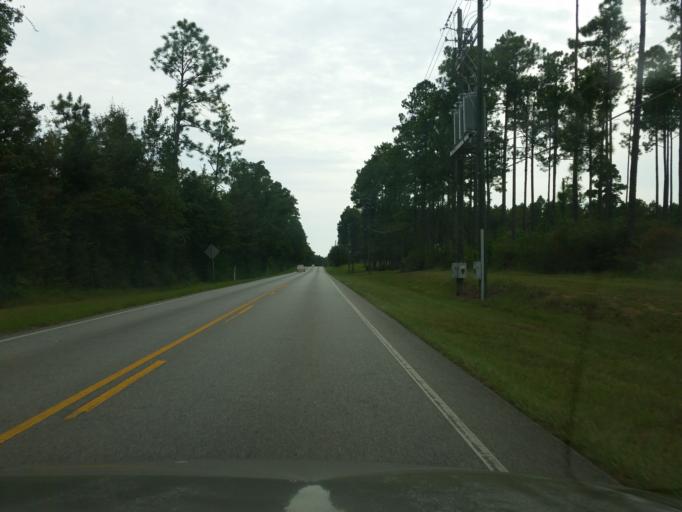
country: US
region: Florida
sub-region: Escambia County
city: Molino
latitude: 30.6759
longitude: -87.3192
